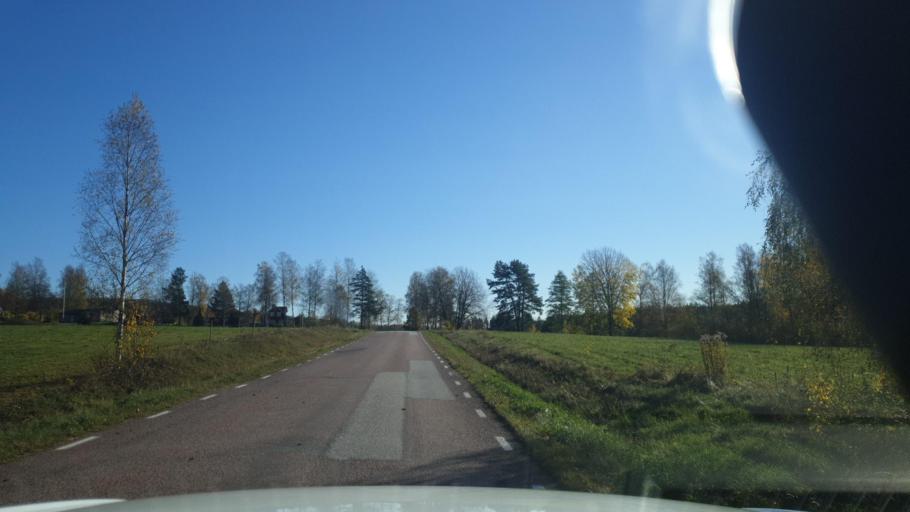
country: SE
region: Vaermland
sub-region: Arvika Kommun
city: Arvika
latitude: 59.5369
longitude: 12.7994
